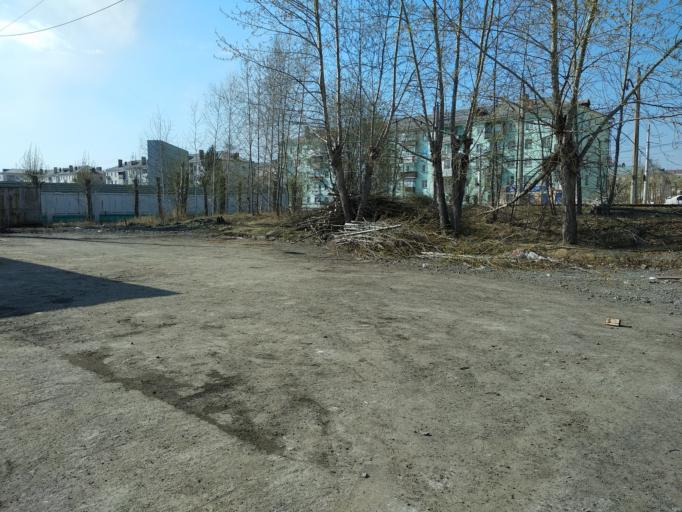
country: RU
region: Sverdlovsk
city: Krasnotur'insk
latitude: 59.7599
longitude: 60.2004
